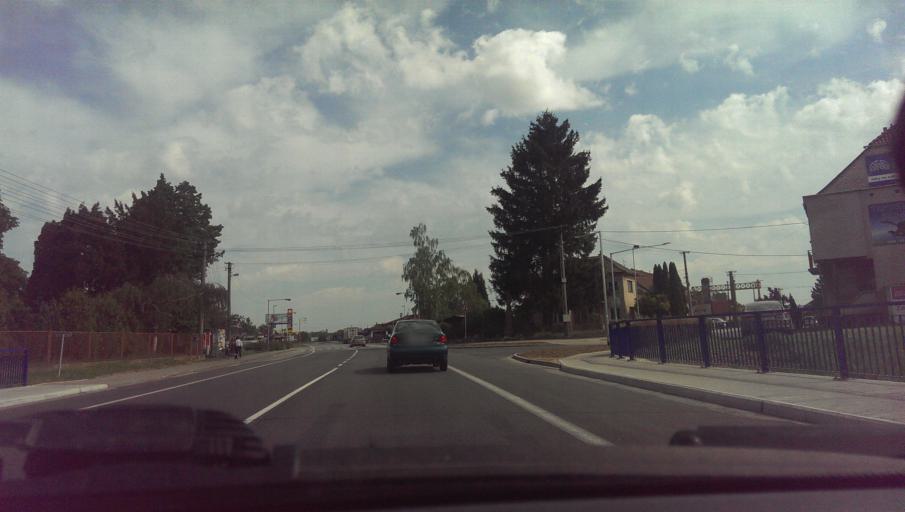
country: CZ
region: Zlin
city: Babice
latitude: 49.1210
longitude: 17.4744
